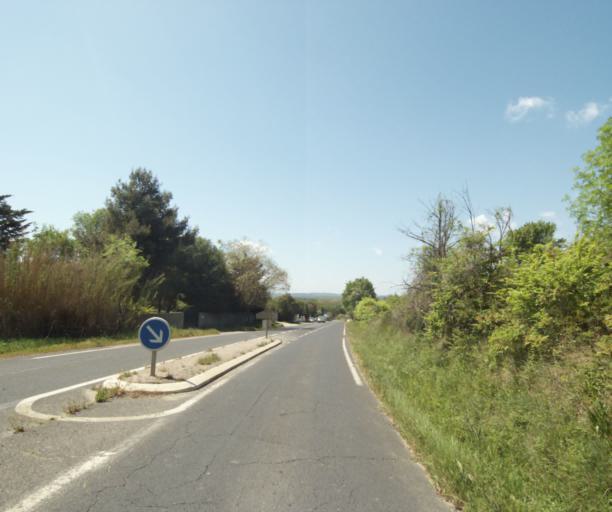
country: FR
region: Languedoc-Roussillon
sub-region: Departement de l'Herault
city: Saint-Jean-de-Vedas
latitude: 43.5927
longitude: 3.8282
